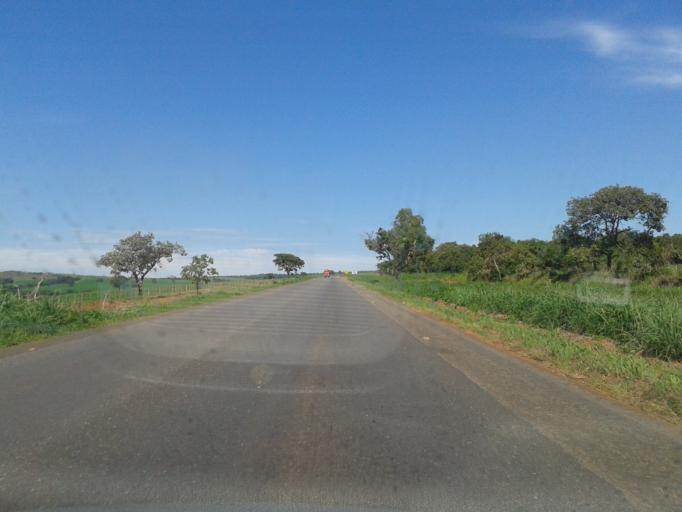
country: BR
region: Goias
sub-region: Bela Vista De Goias
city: Bela Vista de Goias
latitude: -17.1643
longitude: -48.7753
